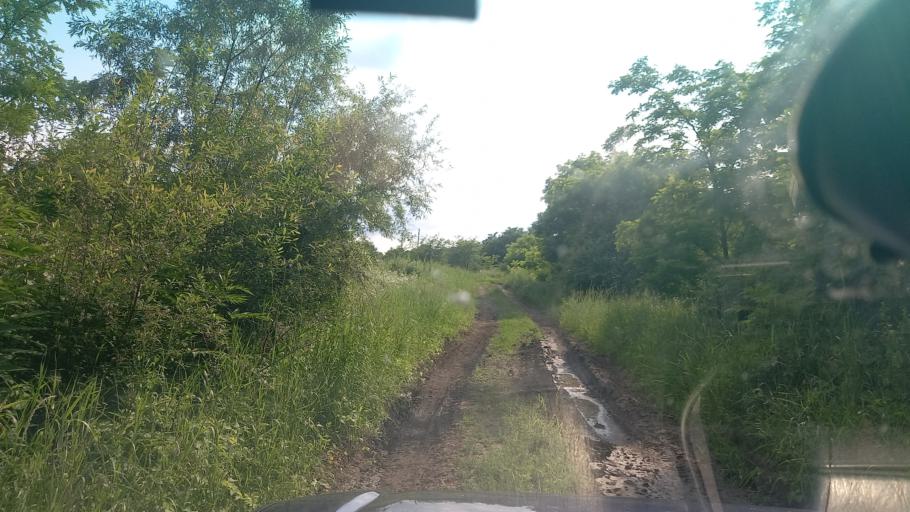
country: RU
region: Adygeya
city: Giaginskaya
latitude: 44.9539
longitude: 40.1075
